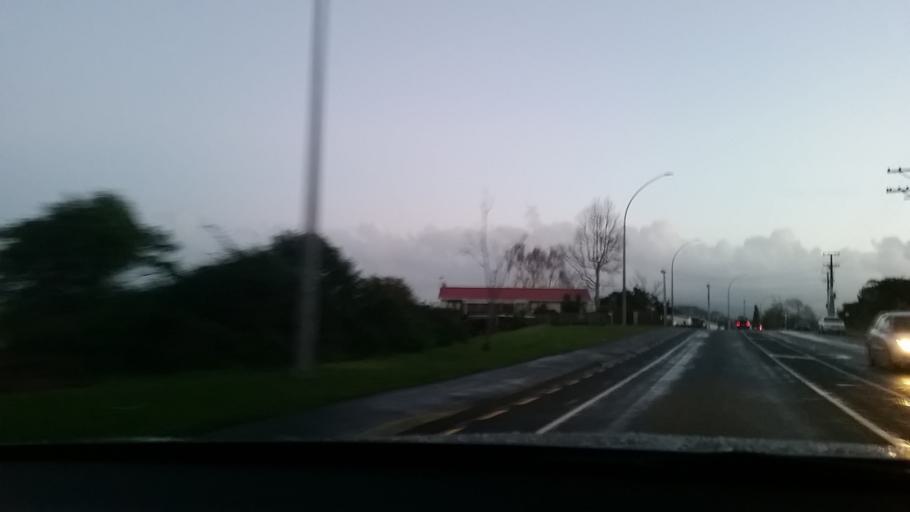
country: NZ
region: Waikato
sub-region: Hamilton City
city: Hamilton
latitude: -37.8015
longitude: 175.2458
